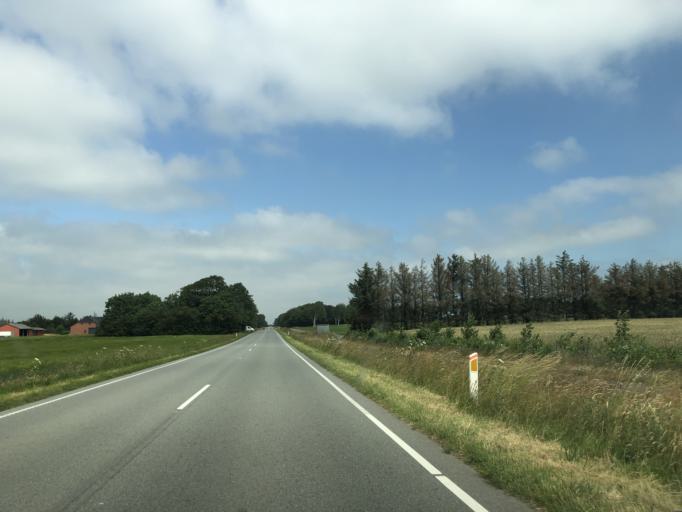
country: DK
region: South Denmark
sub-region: Varde Kommune
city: Varde
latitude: 55.6446
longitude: 8.4871
